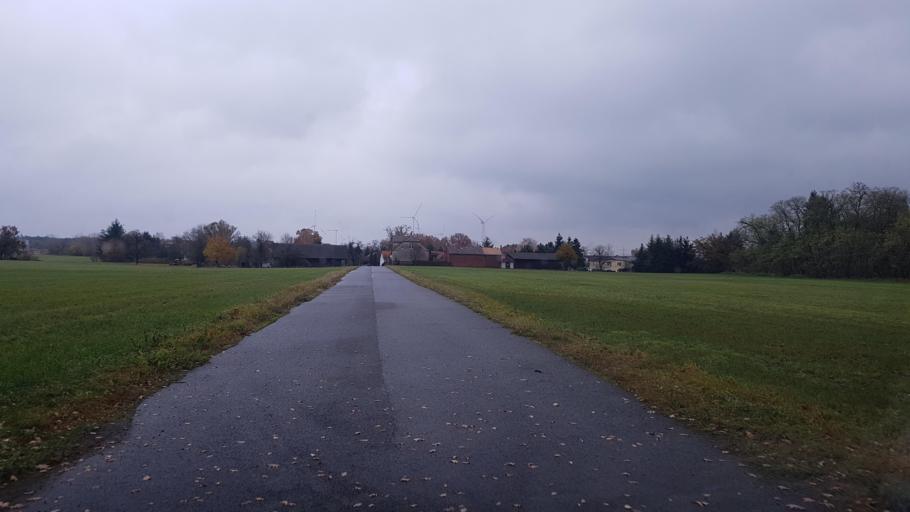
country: DE
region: Brandenburg
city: Drebkau
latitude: 51.6645
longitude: 14.2477
